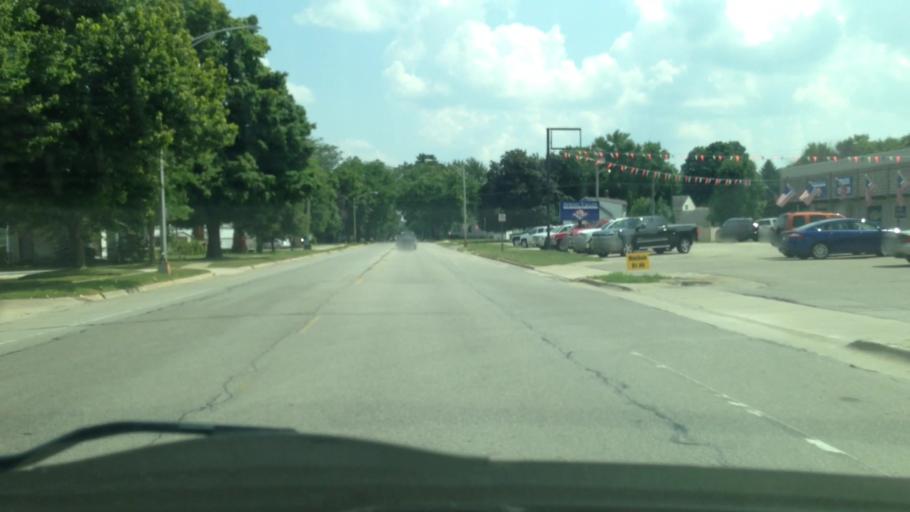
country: US
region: Minnesota
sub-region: Fillmore County
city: Spring Valley
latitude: 43.6958
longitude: -92.3960
